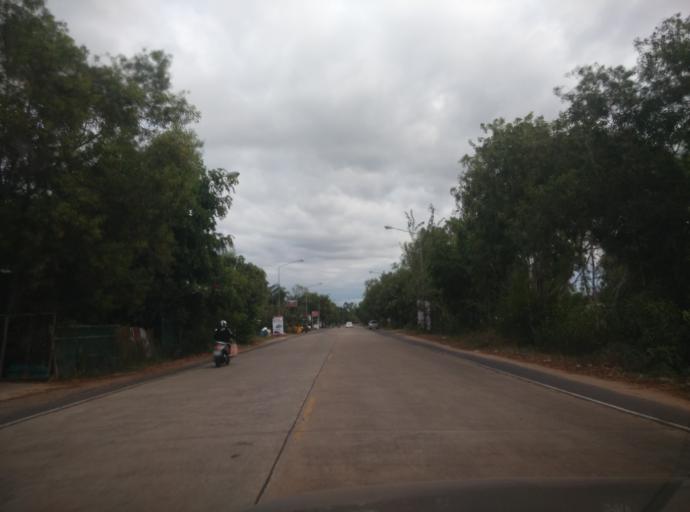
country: TH
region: Sisaket
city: Si Sa Ket
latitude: 15.1208
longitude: 104.3505
